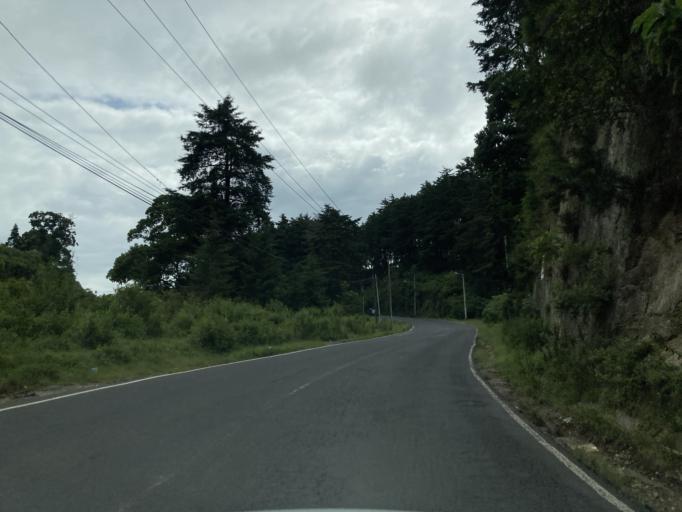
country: GT
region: Guatemala
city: San Jose Pinula
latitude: 14.5352
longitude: -90.4081
